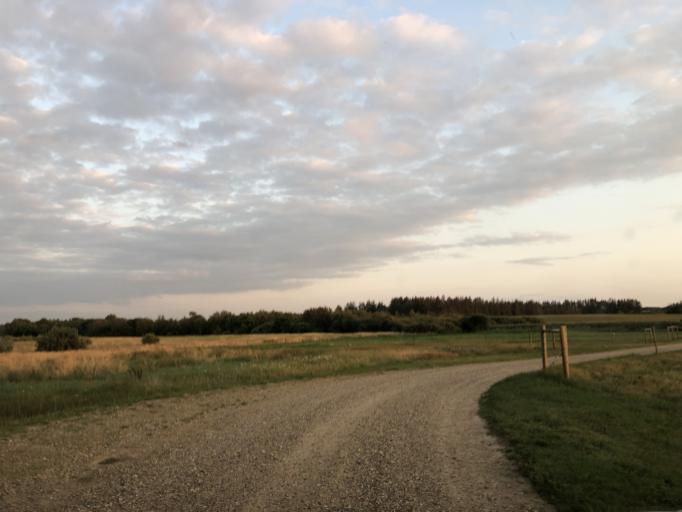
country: DK
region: Central Jutland
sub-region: Holstebro Kommune
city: Vinderup
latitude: 56.4605
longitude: 8.8969
